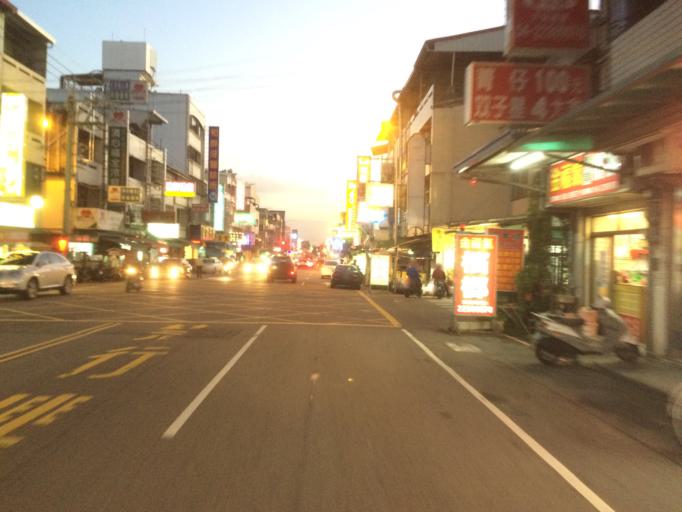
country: TW
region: Taiwan
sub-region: Taichung City
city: Taichung
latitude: 24.1781
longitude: 120.7193
